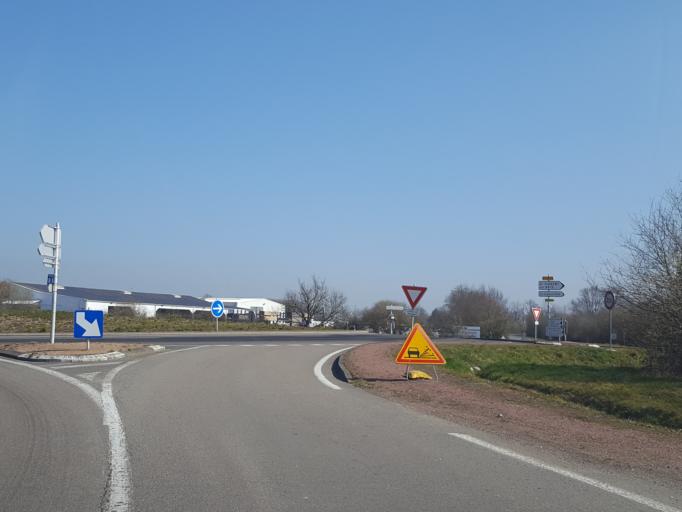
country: FR
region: Pays de la Loire
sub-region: Departement de la Vendee
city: La Chaize-le-Vicomte
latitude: 46.6650
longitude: -1.3421
